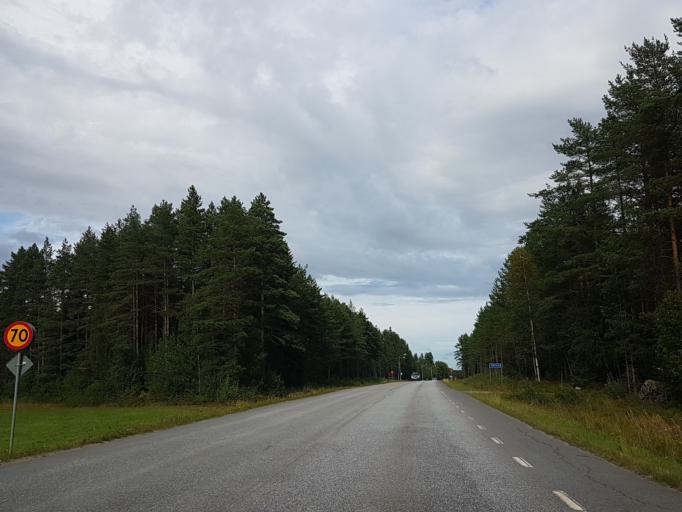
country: SE
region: Vaesterbotten
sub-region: Umea Kommun
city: Taftea
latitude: 63.8331
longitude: 20.4685
